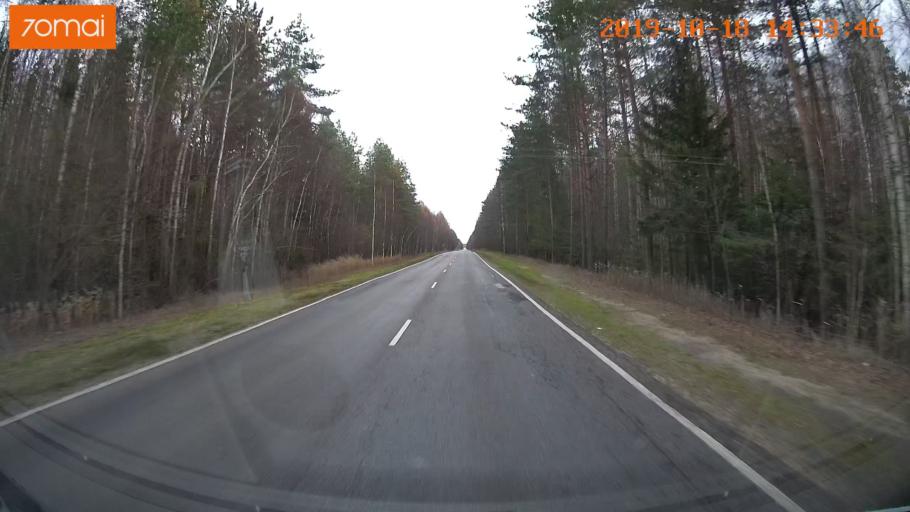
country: RU
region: Rjazan
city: Tuma
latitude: 55.2051
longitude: 40.6032
